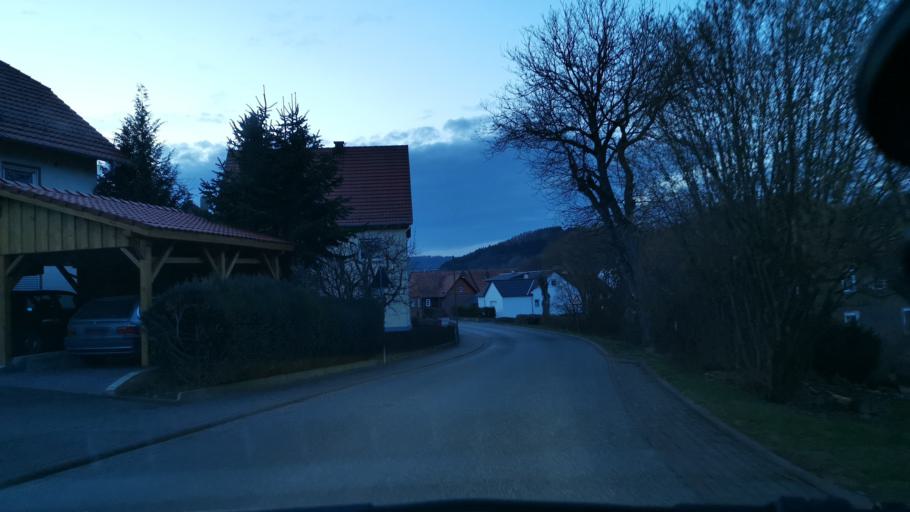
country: DE
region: Hesse
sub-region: Regierungsbezirk Kassel
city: Cornberg
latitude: 51.0516
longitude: 9.8548
